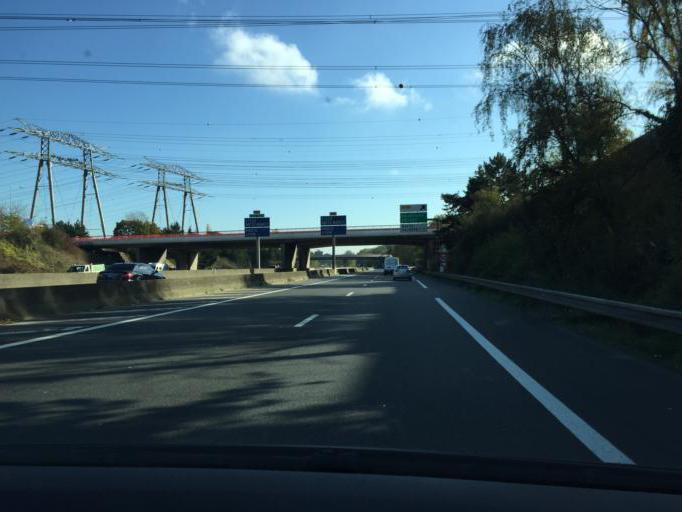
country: FR
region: Ile-de-France
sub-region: Departement de l'Essonne
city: Palaiseau
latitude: 48.7162
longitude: 2.2652
